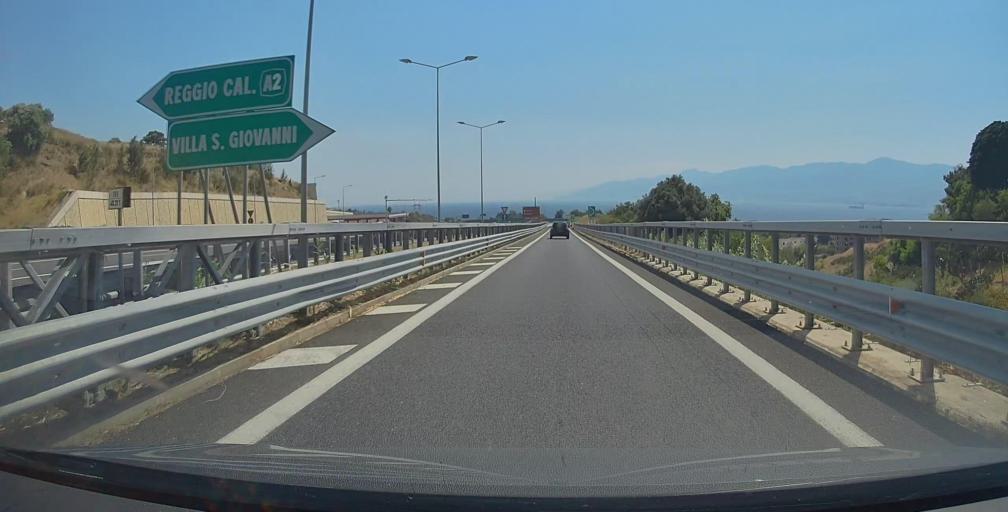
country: IT
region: Calabria
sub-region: Provincia di Reggio Calabria
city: Campo Calabro
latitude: 38.2113
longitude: 15.6449
